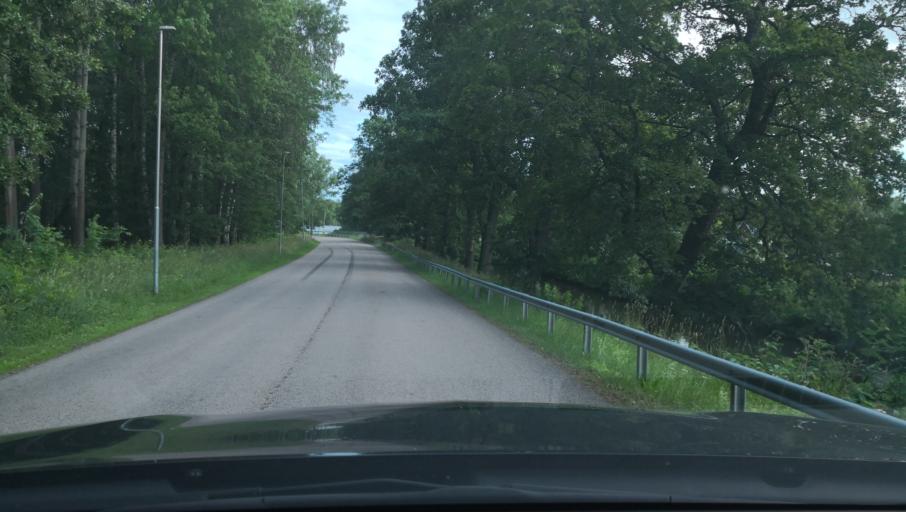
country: SE
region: Vaestmanland
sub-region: Hallstahammars Kommun
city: Hallstahammar
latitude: 59.6183
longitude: 16.2075
